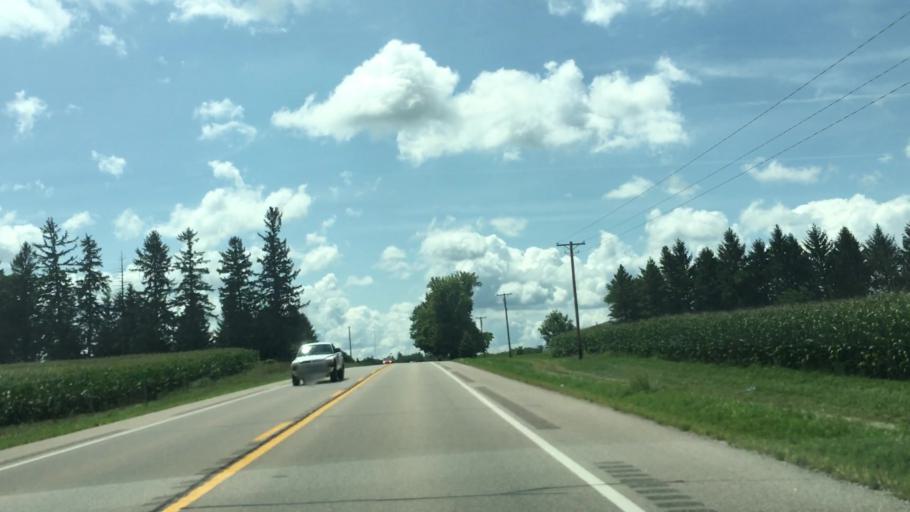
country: US
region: Iowa
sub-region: Johnson County
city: Solon
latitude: 41.8185
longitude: -91.4963
